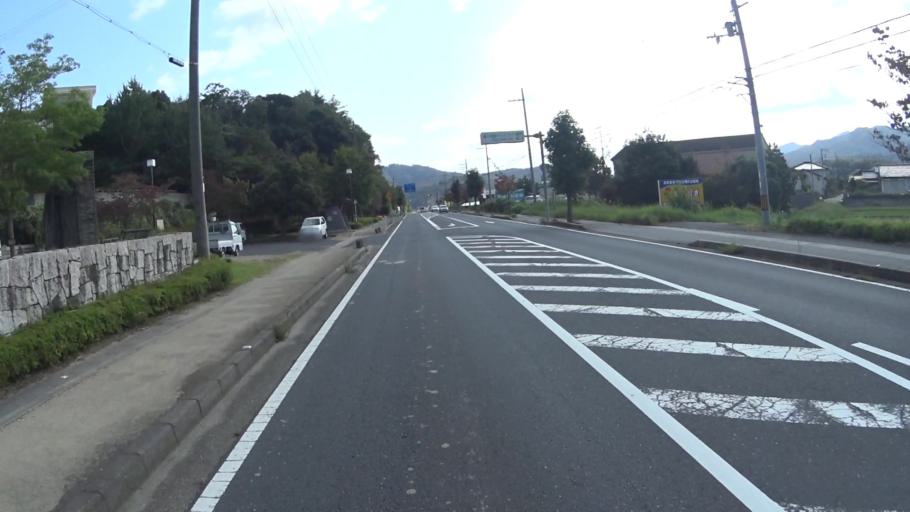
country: JP
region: Kyoto
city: Miyazu
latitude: 35.5807
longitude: 135.0999
